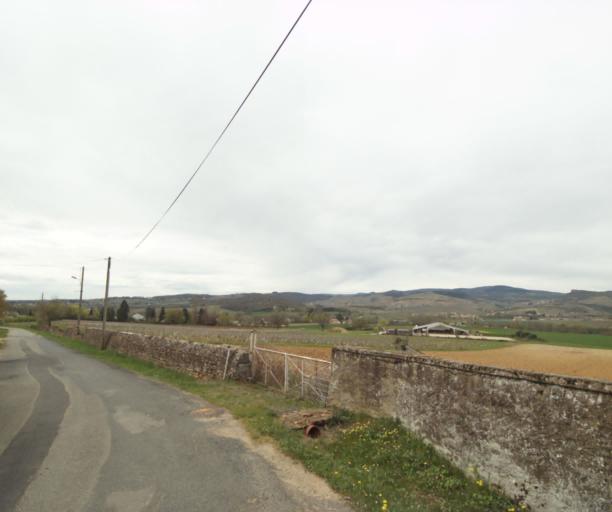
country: FR
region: Bourgogne
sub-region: Departement de Saone-et-Loire
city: Charnay-les-Macon
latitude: 46.3068
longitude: 4.7794
